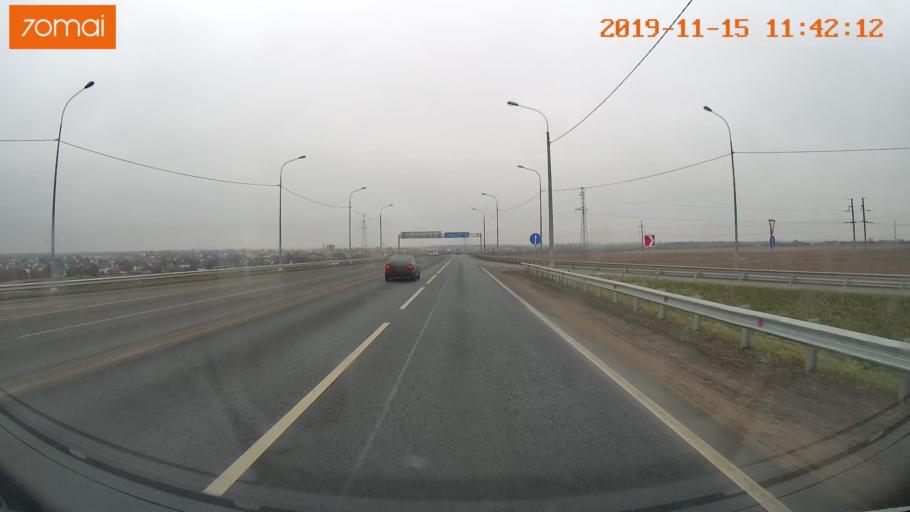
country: RU
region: Vologda
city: Vologda
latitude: 59.2158
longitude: 39.7714
